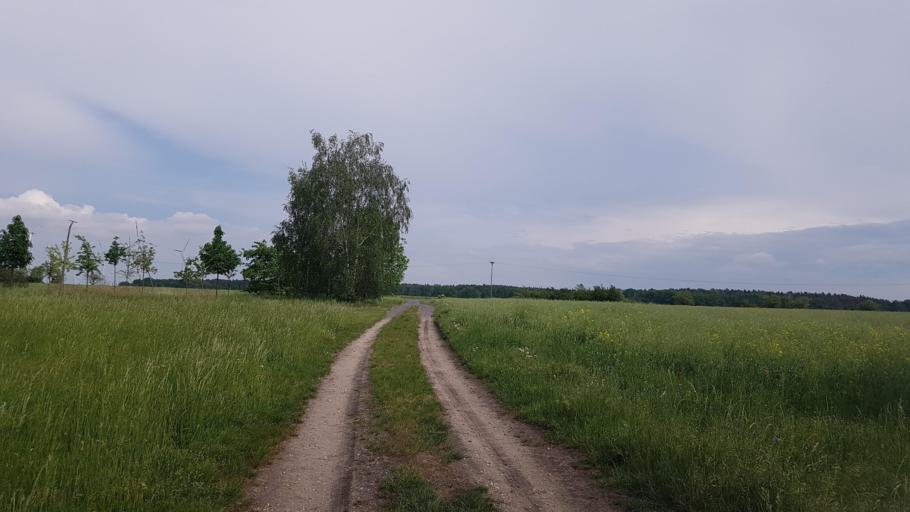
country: DE
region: Brandenburg
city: Sallgast
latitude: 51.5996
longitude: 13.8564
